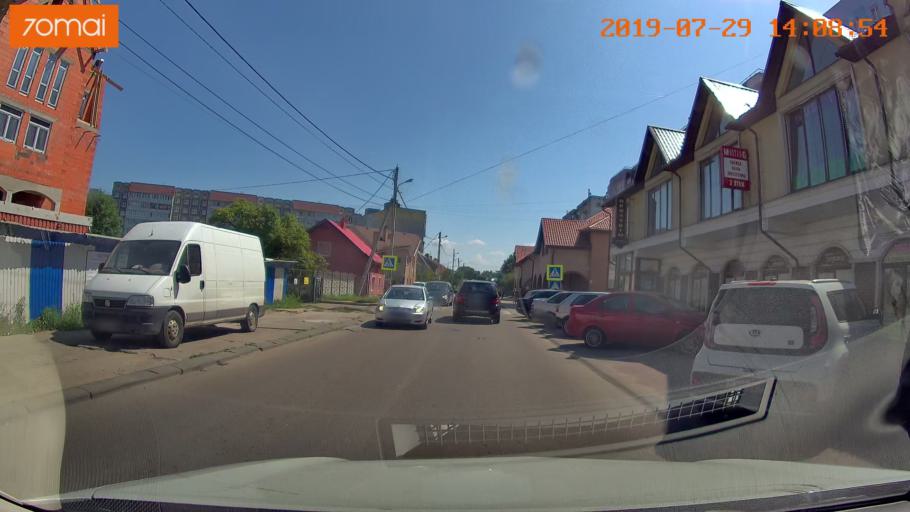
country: RU
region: Kaliningrad
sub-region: Gorod Kaliningrad
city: Baltiysk
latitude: 54.6565
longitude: 19.9080
